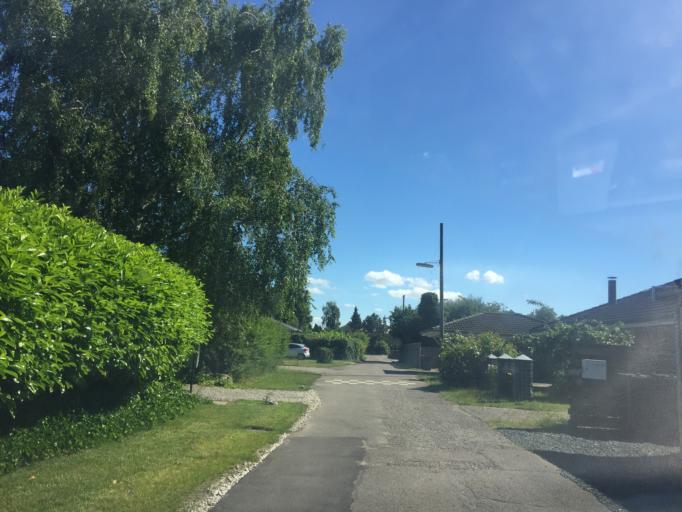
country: DK
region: Capital Region
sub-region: Halsnaes Kommune
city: Liseleje
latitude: 56.0094
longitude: 11.9947
